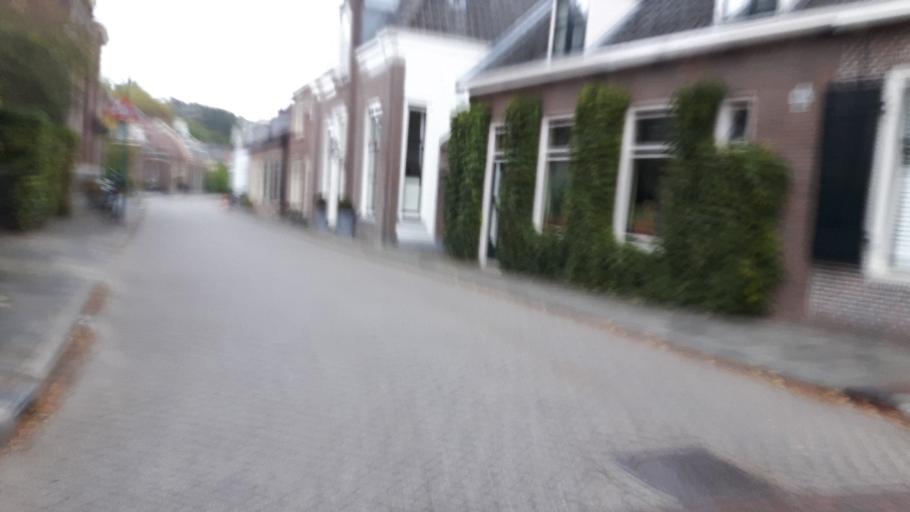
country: NL
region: Utrecht
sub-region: Stichtse Vecht
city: Maarssen
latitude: 52.1276
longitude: 5.0702
